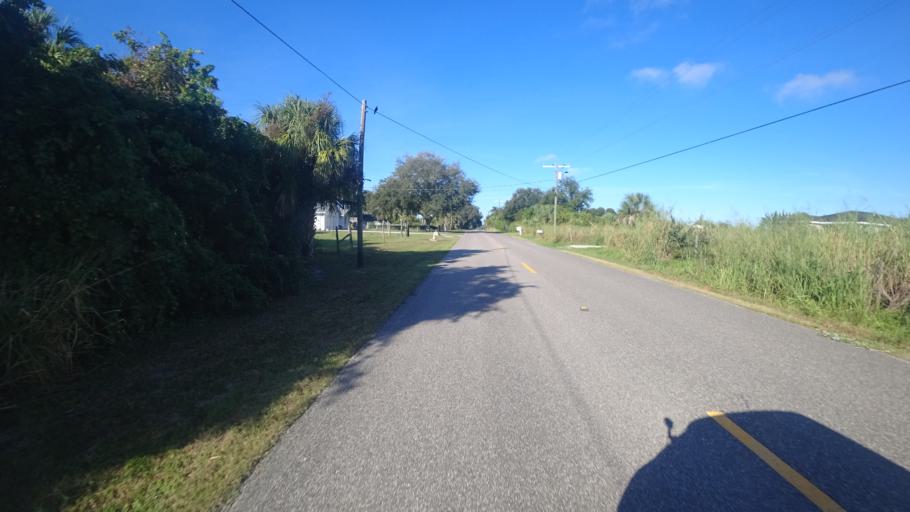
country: US
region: Florida
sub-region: Manatee County
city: Memphis
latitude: 27.5903
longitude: -82.5300
